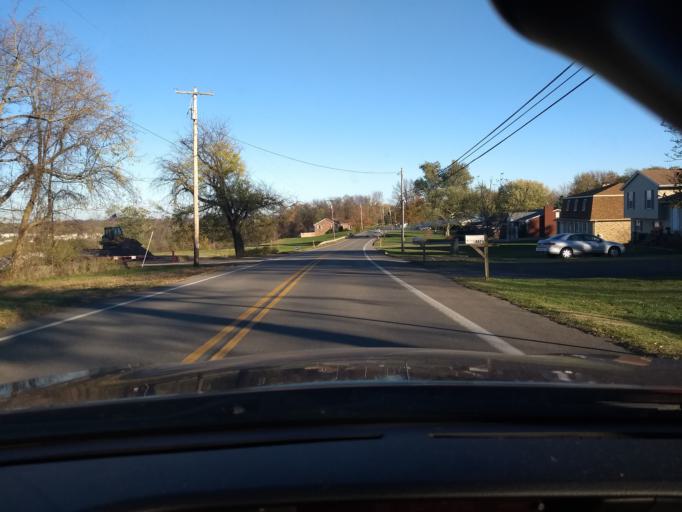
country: US
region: Pennsylvania
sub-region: Allegheny County
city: Oakdale
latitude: 40.3811
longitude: -80.1704
